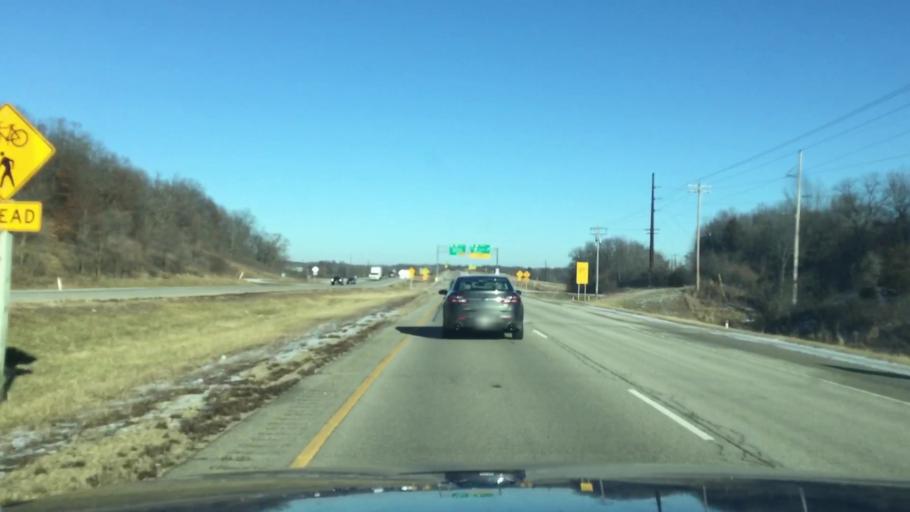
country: US
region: Wisconsin
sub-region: Racine County
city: Browns Lake
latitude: 42.7131
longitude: -88.2324
